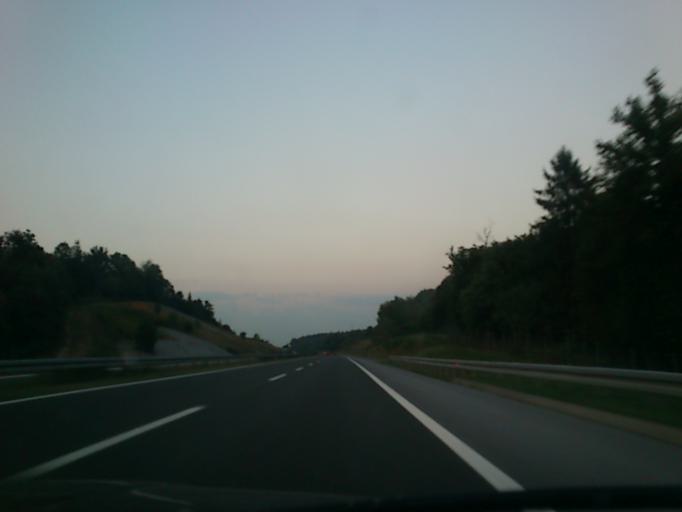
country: HR
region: Karlovacka
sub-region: Grad Ogulin
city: Ogulin
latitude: 45.4288
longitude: 15.3142
